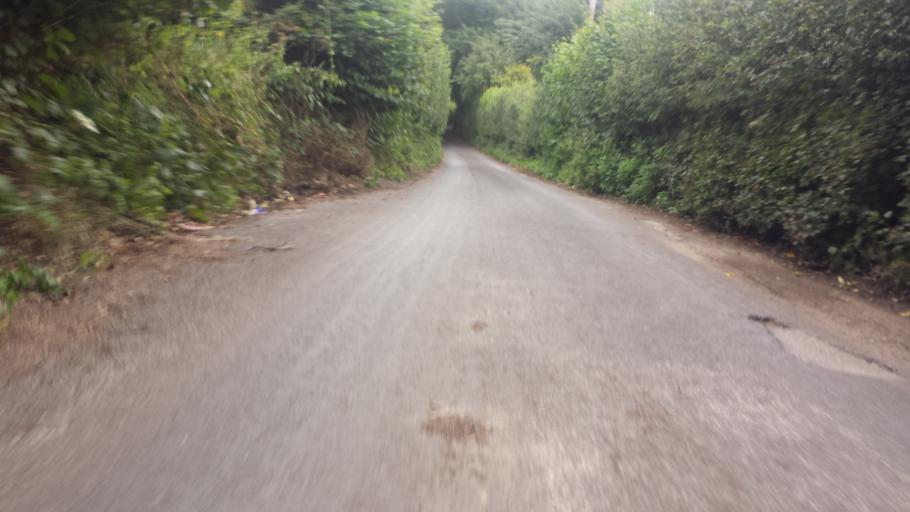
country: GB
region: England
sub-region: Kent
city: Swanley
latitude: 51.3705
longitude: 0.1559
